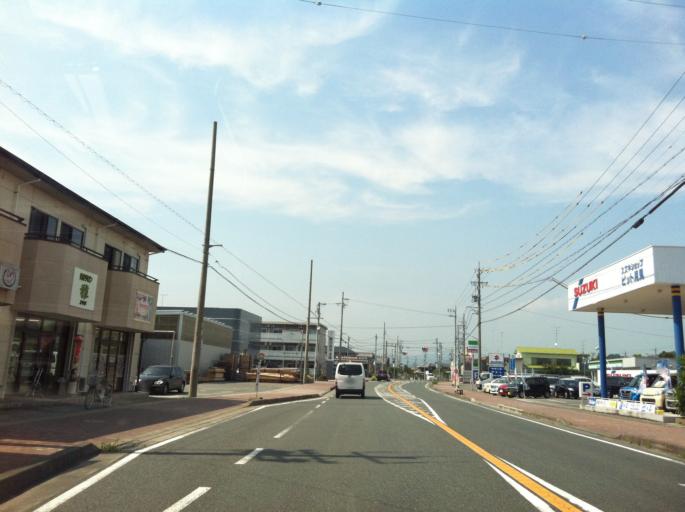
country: JP
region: Shizuoka
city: Fukuroi
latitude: 34.7843
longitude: 137.9085
